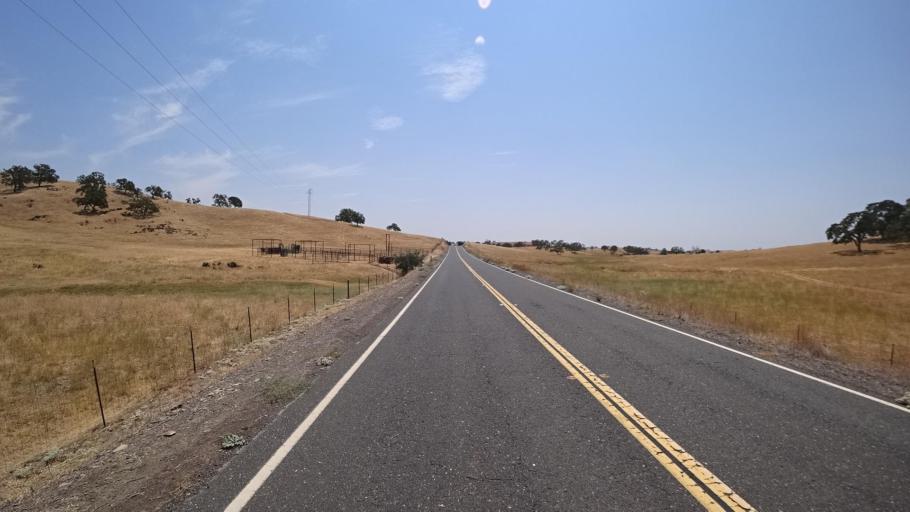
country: US
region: California
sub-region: Tuolumne County
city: Jamestown
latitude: 37.6367
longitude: -120.3714
